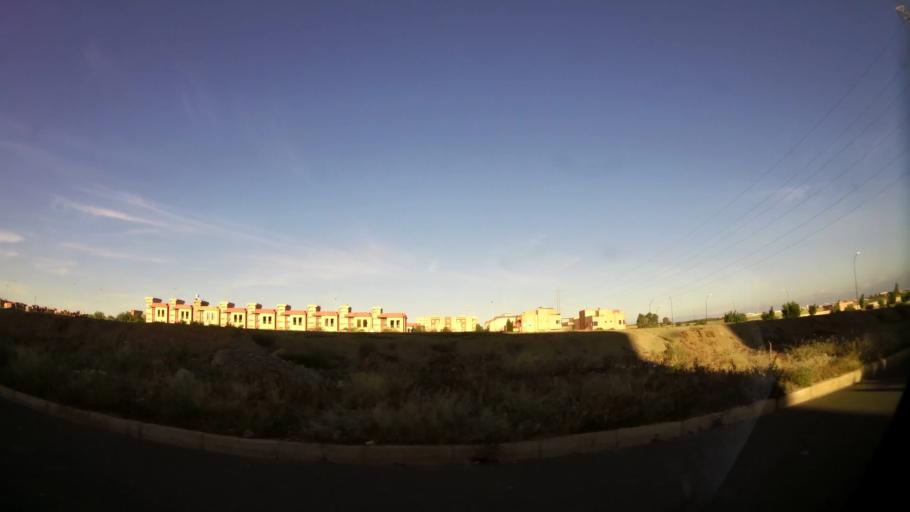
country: MA
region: Marrakech-Tensift-Al Haouz
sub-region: Marrakech
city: Marrakesh
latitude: 31.7434
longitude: -8.1149
